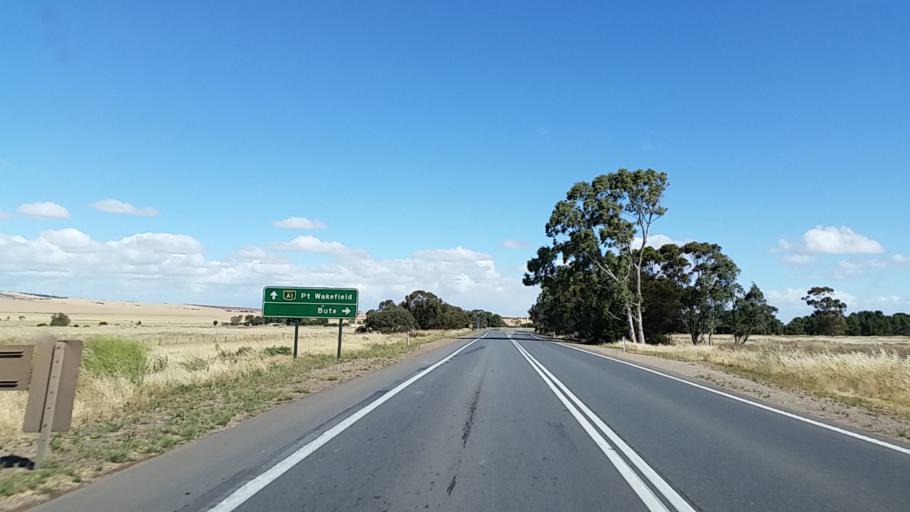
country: AU
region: South Australia
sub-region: Clare and Gilbert Valleys
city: Clare
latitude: -33.7911
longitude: 138.2083
